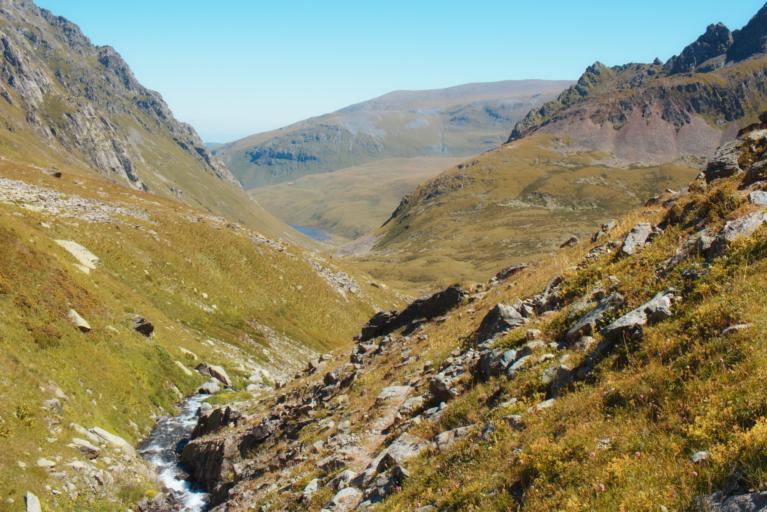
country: RU
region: Karachayevo-Cherkesiya
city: Mednogorskiy
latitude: 43.6227
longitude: 41.1127
